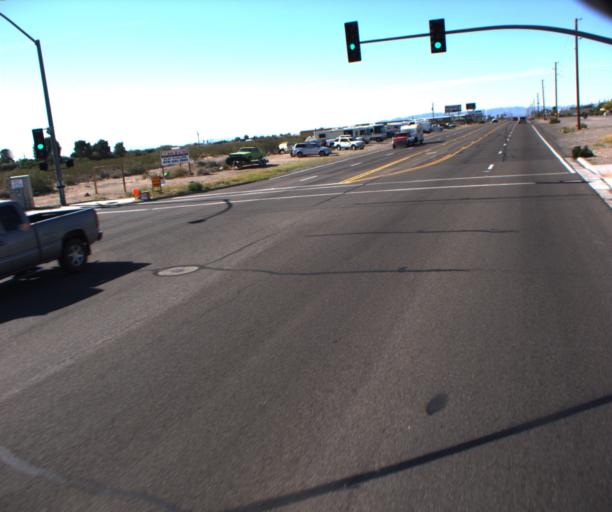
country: US
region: Arizona
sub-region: Mohave County
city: Mohave Valley
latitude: 34.9971
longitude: -114.5981
